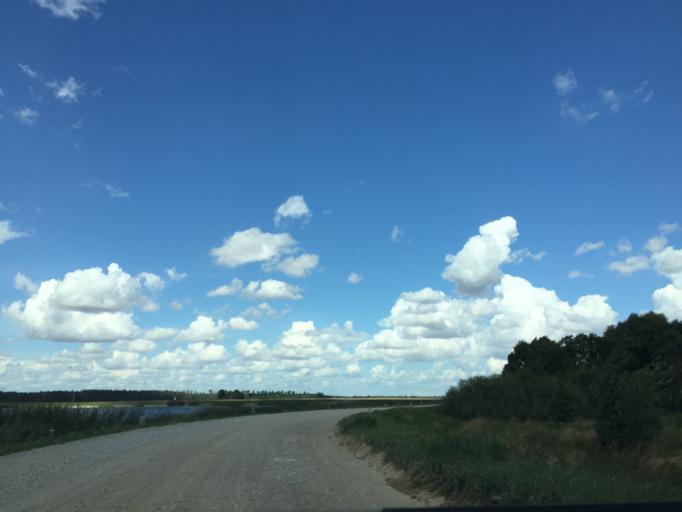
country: LV
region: Rundales
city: Pilsrundale
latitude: 56.3006
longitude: 23.9878
